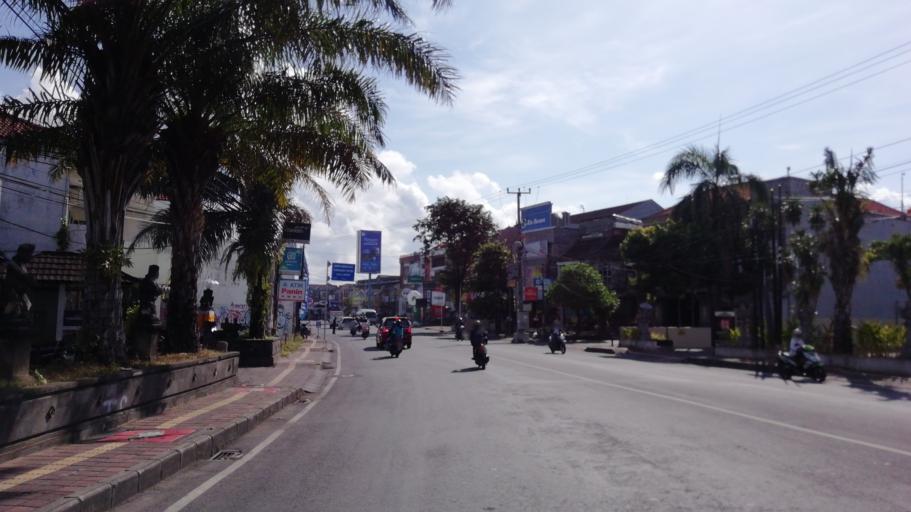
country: ID
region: Bali
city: Denpasar
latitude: -8.6759
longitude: 115.2070
